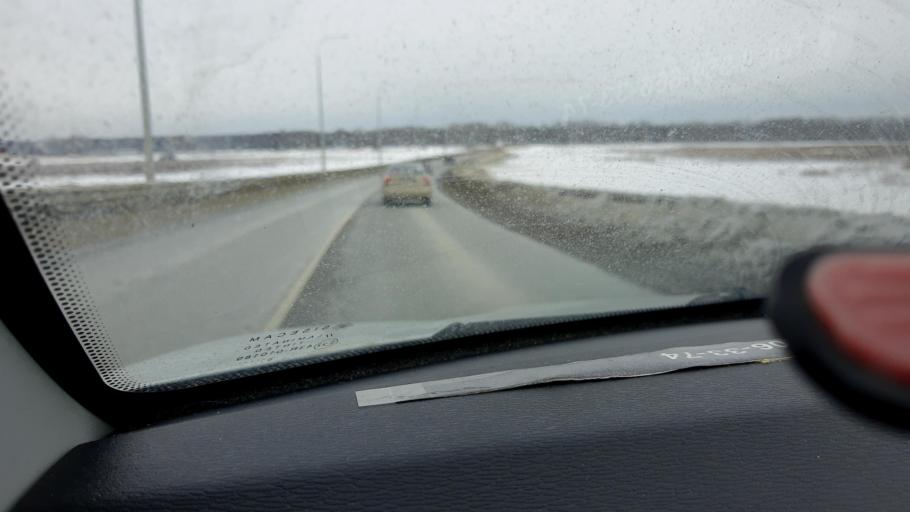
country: RU
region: Nizjnij Novgorod
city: Neklyudovo
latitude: 56.4192
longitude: 43.9874
